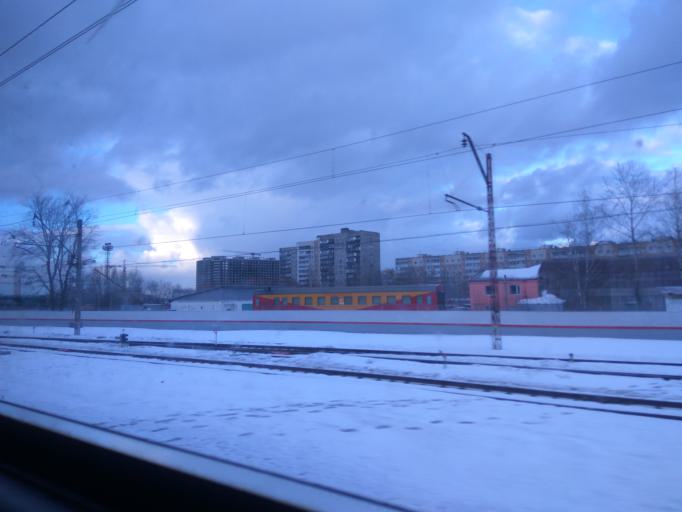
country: RU
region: Moskovskaya
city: Biryulevo Zapadnoye
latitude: 55.5984
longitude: 37.6509
